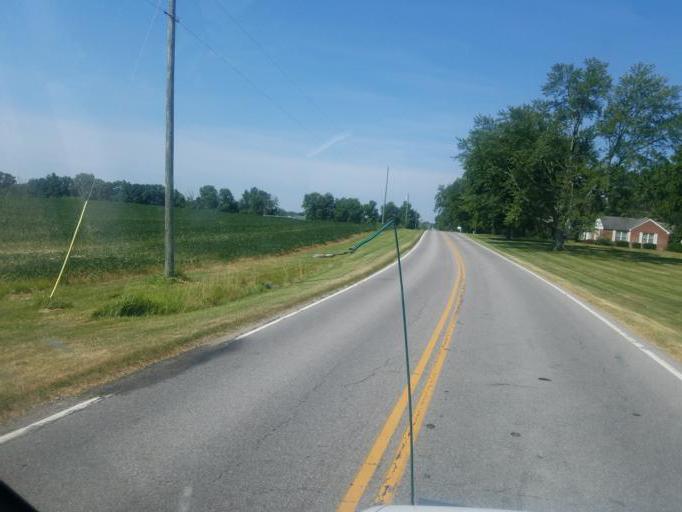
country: US
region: Ohio
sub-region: Union County
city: Marysville
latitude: 40.2273
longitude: -83.4049
